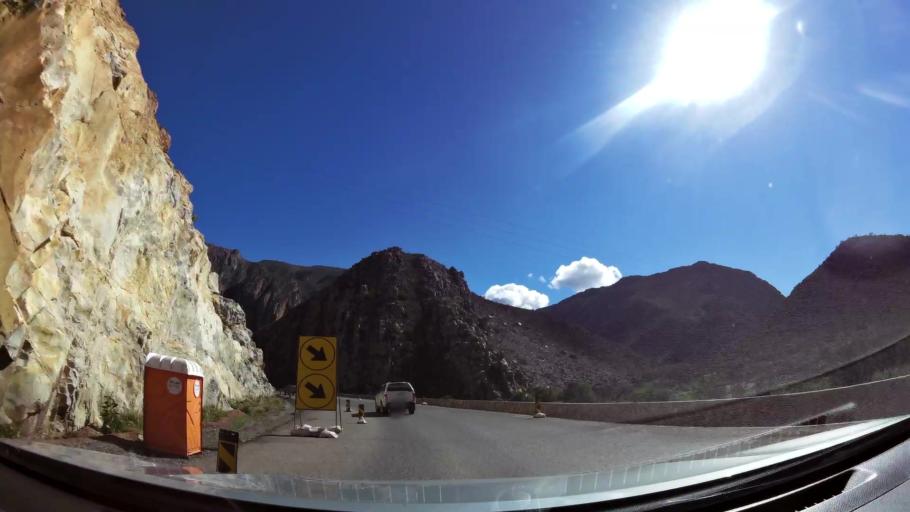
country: ZA
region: Western Cape
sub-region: Cape Winelands District Municipality
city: Ashton
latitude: -33.8034
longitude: 20.1008
